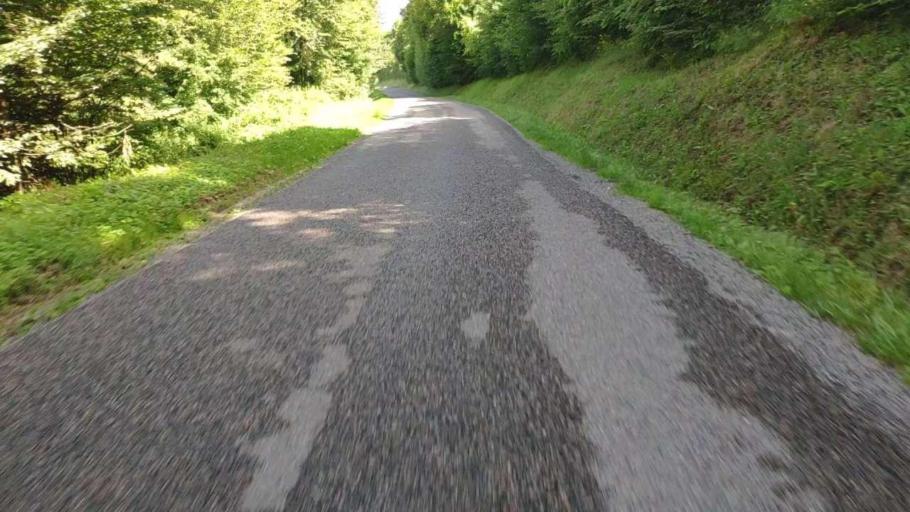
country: FR
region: Franche-Comte
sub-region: Departement du Jura
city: Bletterans
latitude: 46.8093
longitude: 5.5618
